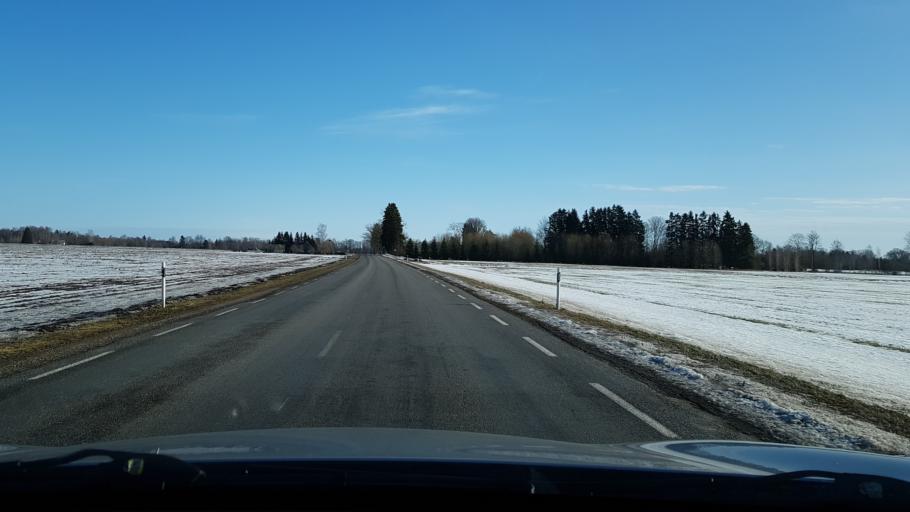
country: EE
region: Viljandimaa
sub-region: Vohma linn
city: Vohma
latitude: 58.6292
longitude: 25.6277
